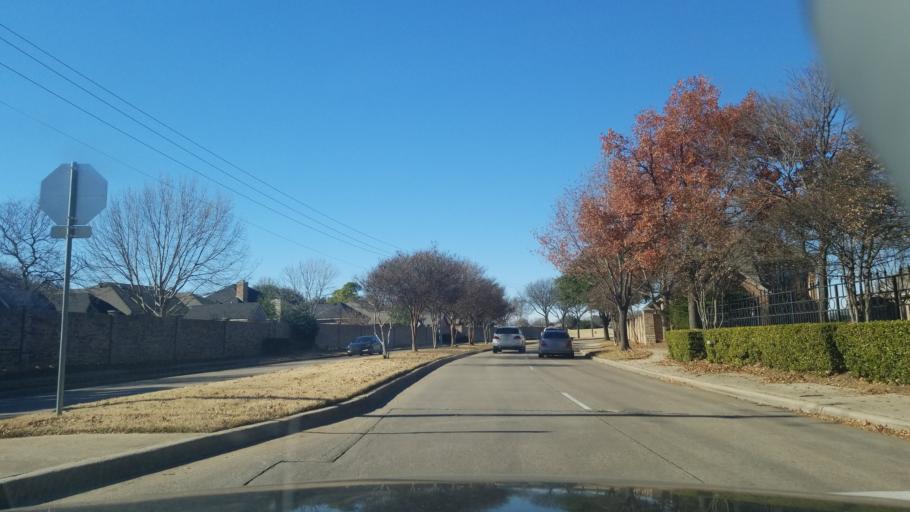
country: US
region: Texas
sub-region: Denton County
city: Corinth
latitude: 33.1554
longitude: -97.0849
